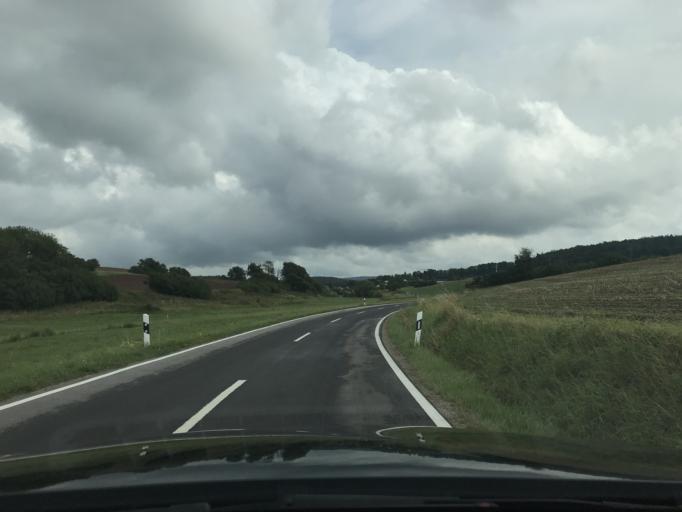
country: DE
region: Bavaria
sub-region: Regierungsbezirk Unterfranken
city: Kirchlauter
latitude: 50.0470
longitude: 10.7032
